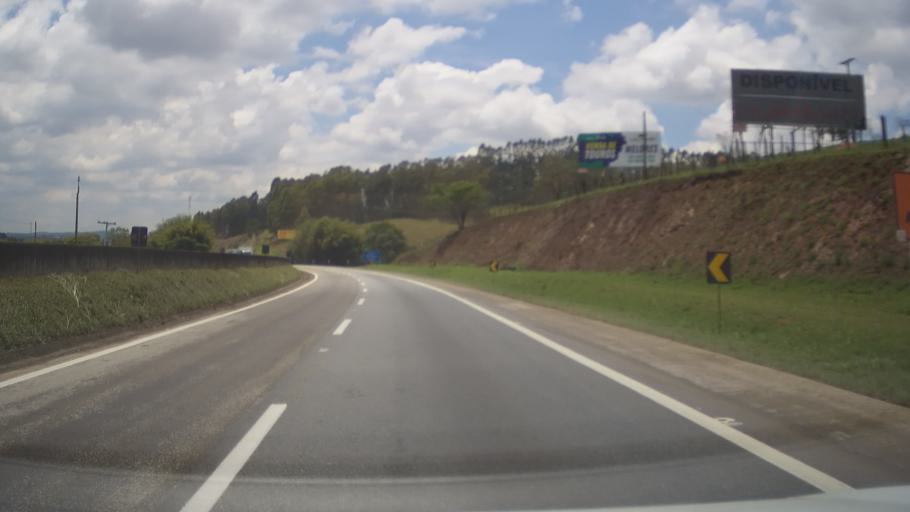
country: BR
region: Minas Gerais
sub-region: Tres Coracoes
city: Tres Coracoes
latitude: -21.6939
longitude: -45.3534
